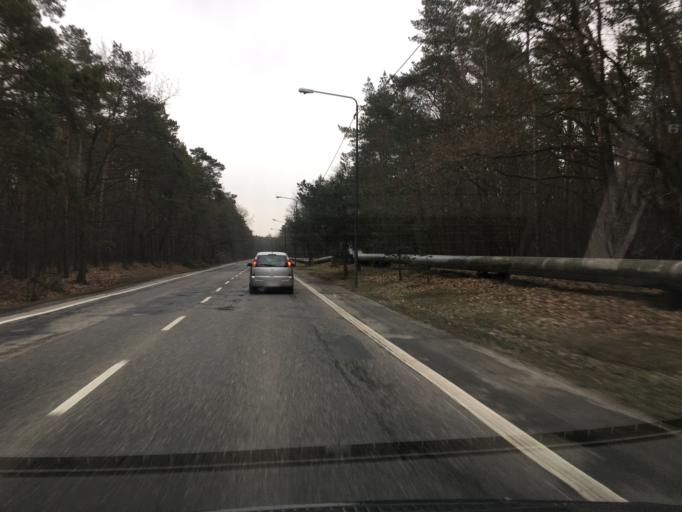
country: PL
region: Opole Voivodeship
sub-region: Powiat kedzierzynsko-kozielski
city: Kedzierzyn-Kozle
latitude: 50.3406
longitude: 18.2274
